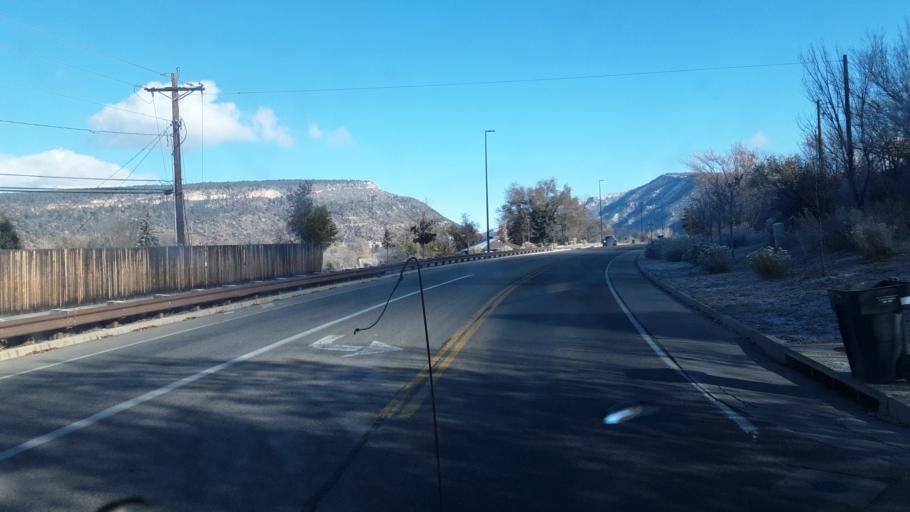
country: US
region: Colorado
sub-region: La Plata County
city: Durango
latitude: 37.2868
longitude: -107.8665
